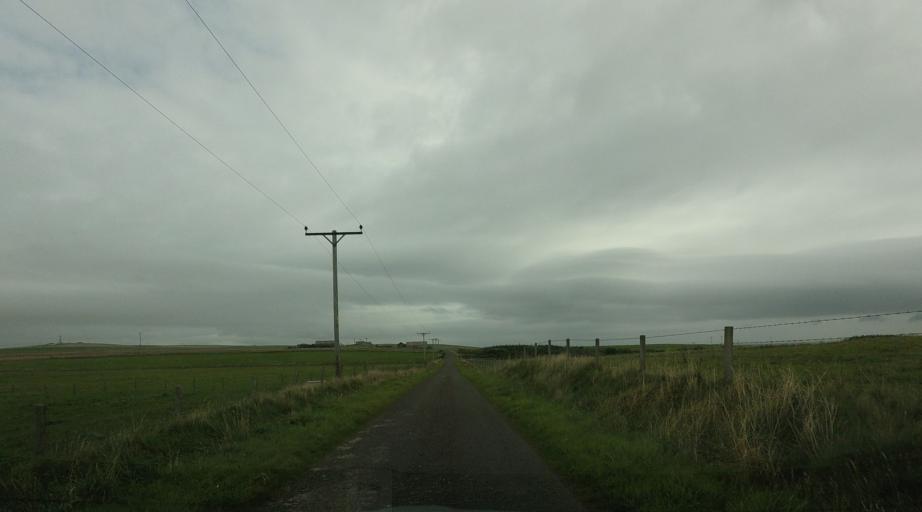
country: GB
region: Scotland
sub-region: Orkney Islands
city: Orkney
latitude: 58.7651
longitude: -2.9580
